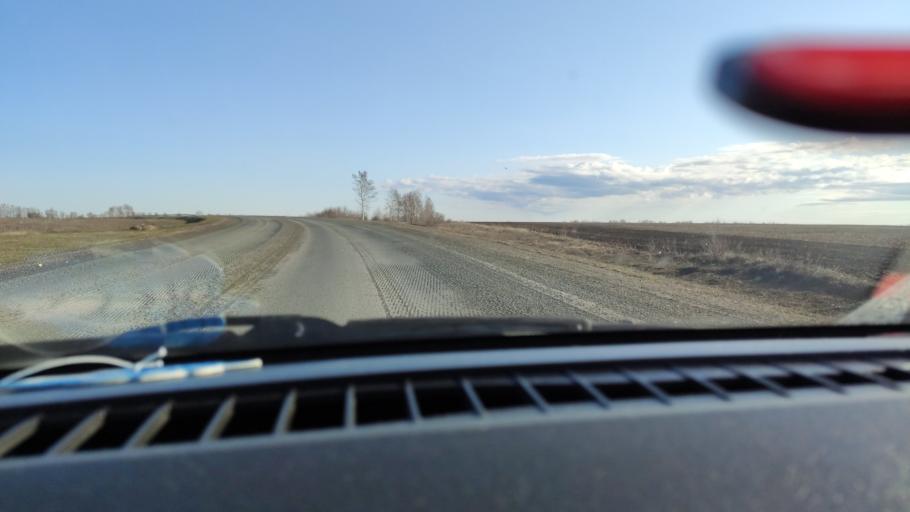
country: RU
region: Saratov
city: Dukhovnitskoye
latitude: 52.7118
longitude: 48.2663
